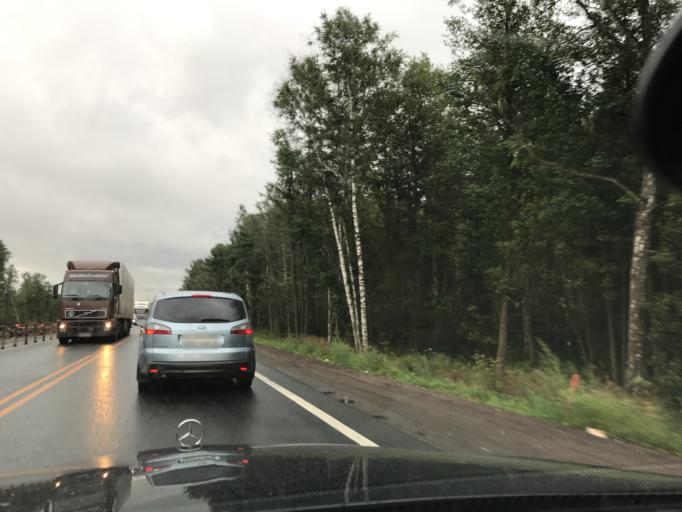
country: RU
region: Moskovskaya
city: Malaya Dubna
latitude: 55.8937
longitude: 39.0351
